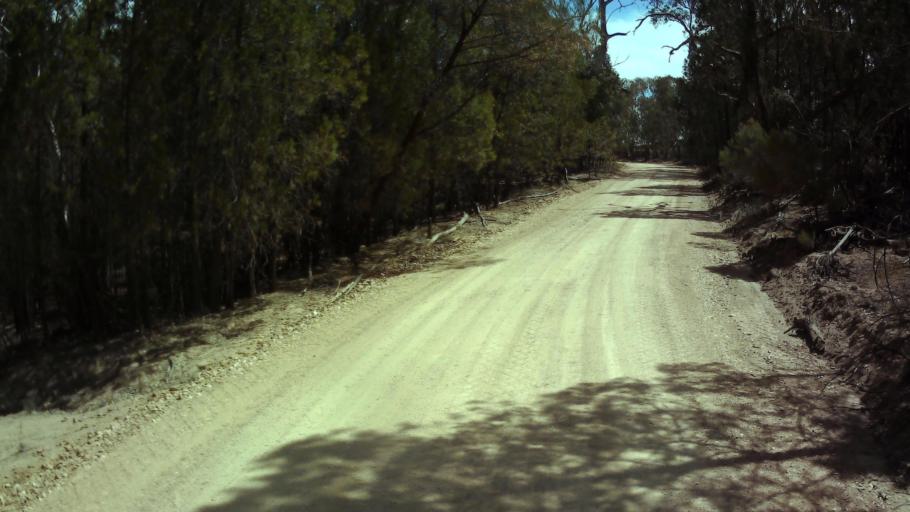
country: AU
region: New South Wales
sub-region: Weddin
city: Grenfell
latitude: -33.8090
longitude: 148.1591
